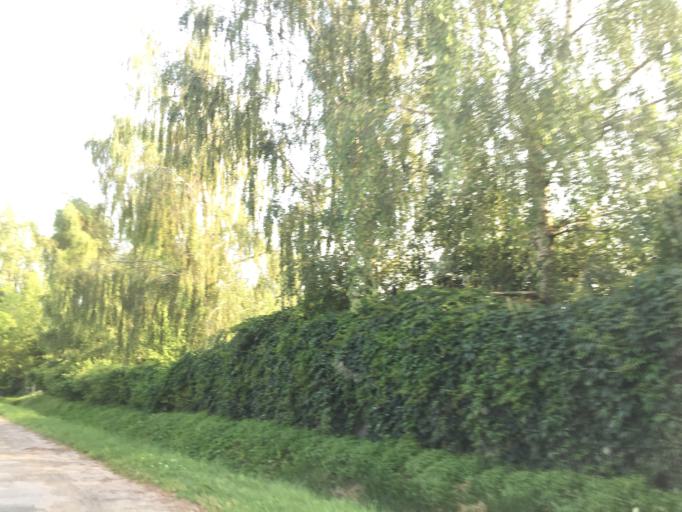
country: LV
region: Jelgava
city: Jelgava
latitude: 56.6652
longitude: 23.6996
